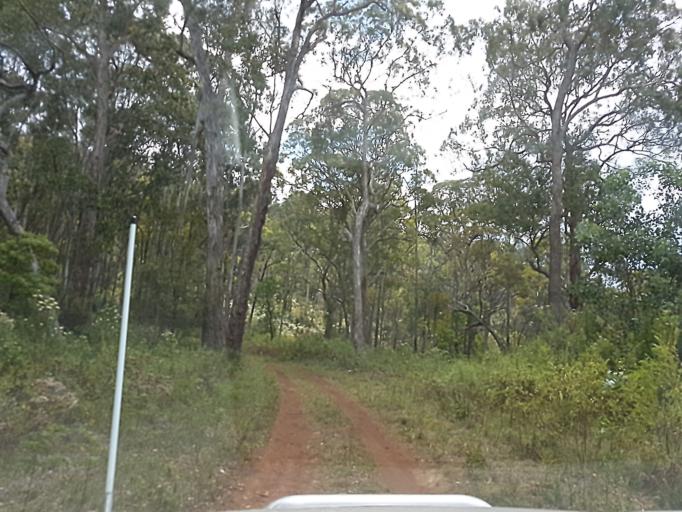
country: AU
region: Victoria
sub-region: East Gippsland
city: Lakes Entrance
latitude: -37.3481
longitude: 148.3578
